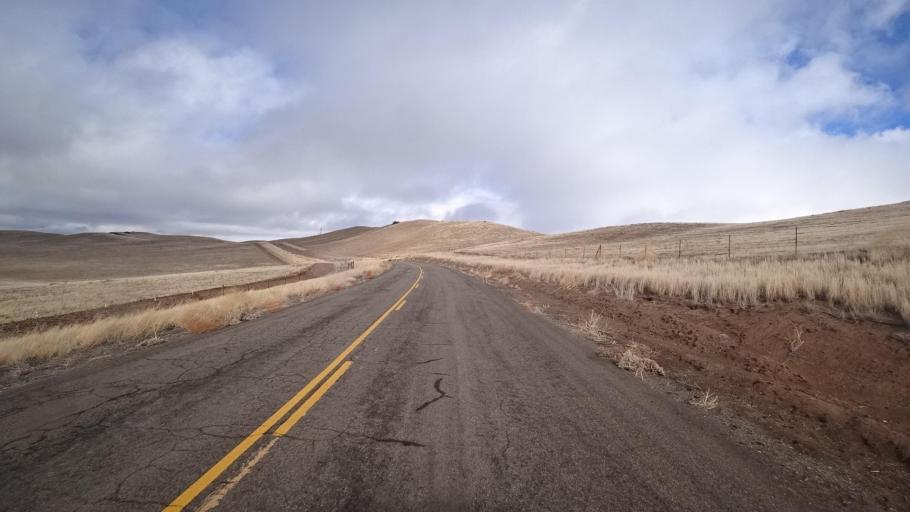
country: US
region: California
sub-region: Kern County
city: Maricopa
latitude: 34.9094
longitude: -119.3952
